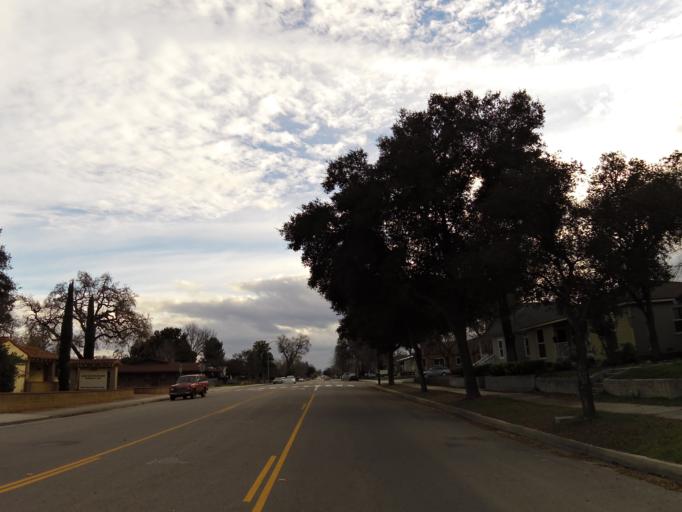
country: US
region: California
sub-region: San Luis Obispo County
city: Paso Robles
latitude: 35.6356
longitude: -120.6922
